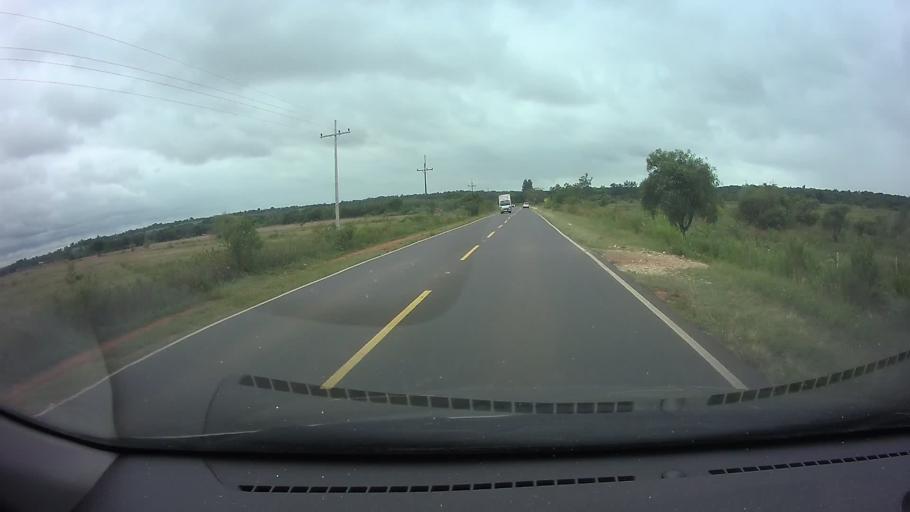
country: PY
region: Central
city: Nueva Italia
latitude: -25.6117
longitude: -57.4516
